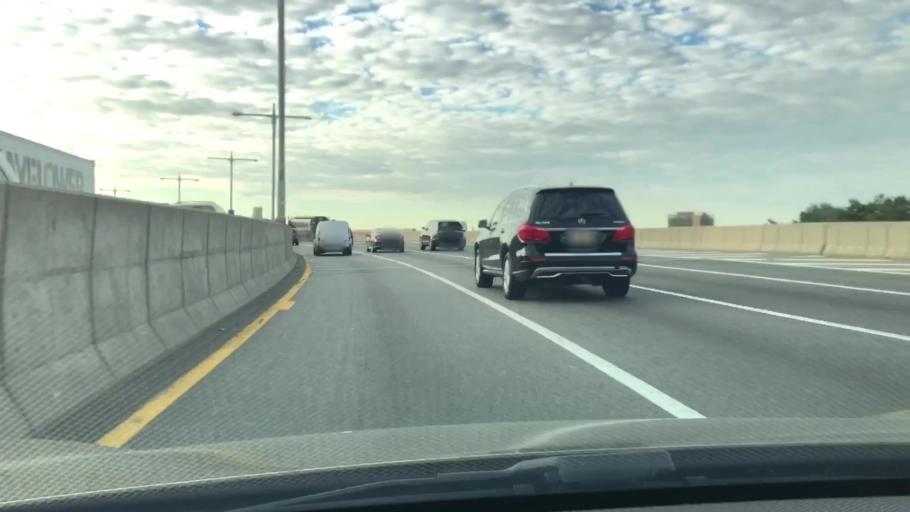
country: US
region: New York
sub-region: New York County
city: Manhattan
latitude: 40.7852
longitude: -73.9302
